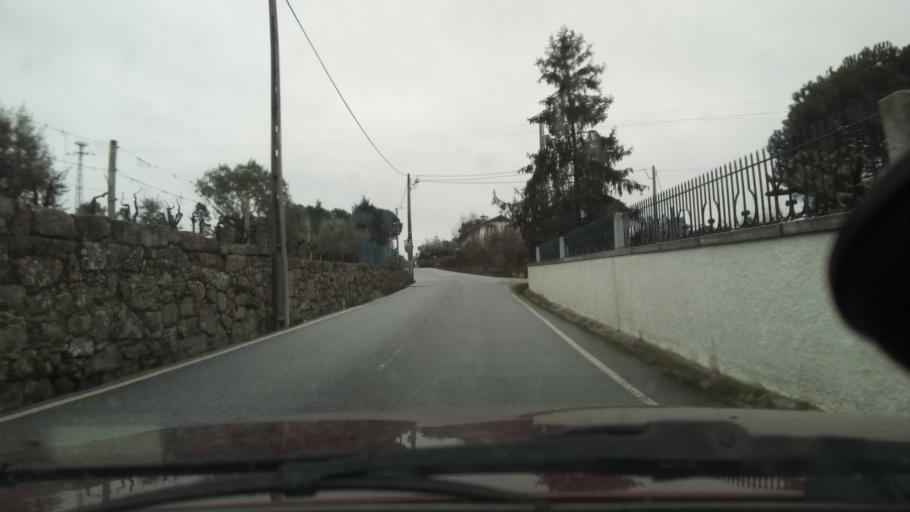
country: PT
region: Viseu
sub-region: Mangualde
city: Mangualde
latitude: 40.6038
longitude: -7.8206
